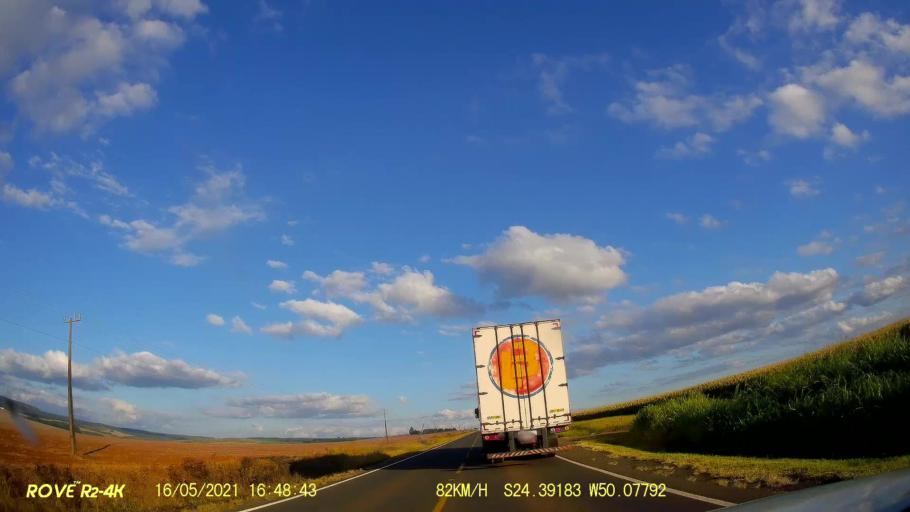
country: BR
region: Parana
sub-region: Pirai Do Sul
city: Pirai do Sul
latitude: -24.3924
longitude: -50.0780
